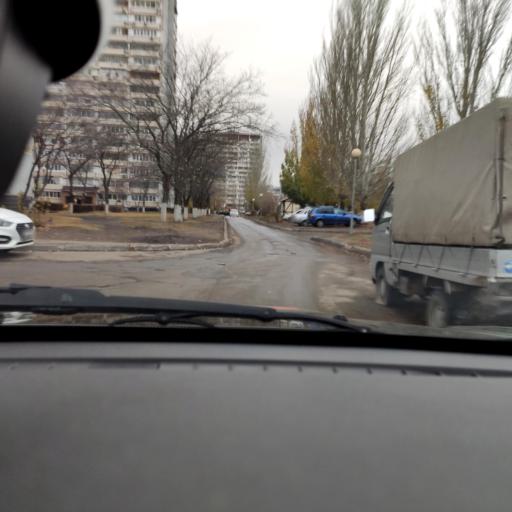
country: RU
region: Samara
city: Tol'yatti
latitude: 53.5365
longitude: 49.3387
